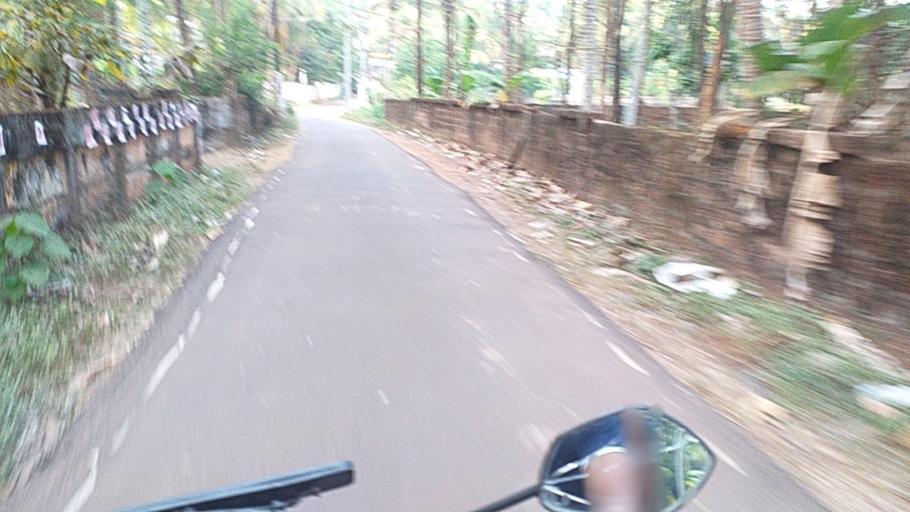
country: IN
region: Kerala
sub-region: Thrissur District
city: Kunnamkulam
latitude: 10.7344
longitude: 76.0448
